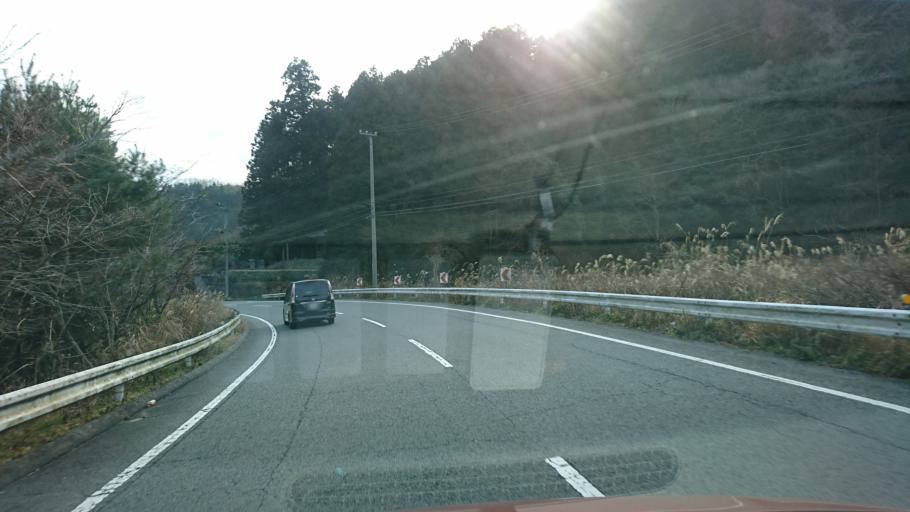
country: JP
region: Ehime
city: Hojo
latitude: 33.9204
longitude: 132.8859
